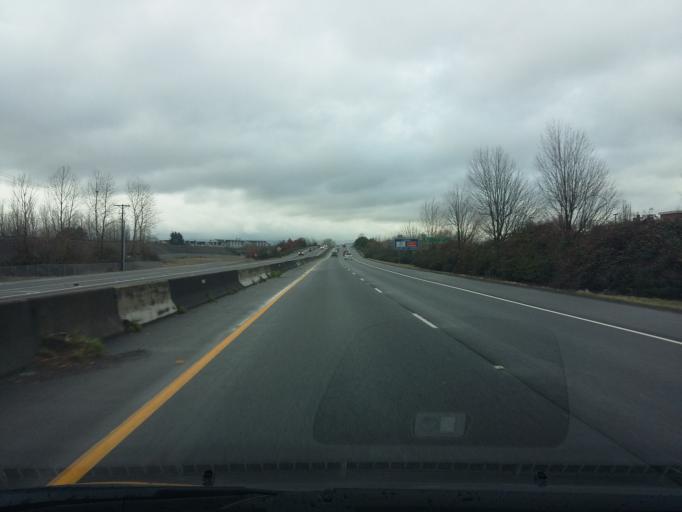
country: US
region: Washington
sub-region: Clark County
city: Vancouver
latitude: 45.6186
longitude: -122.6450
